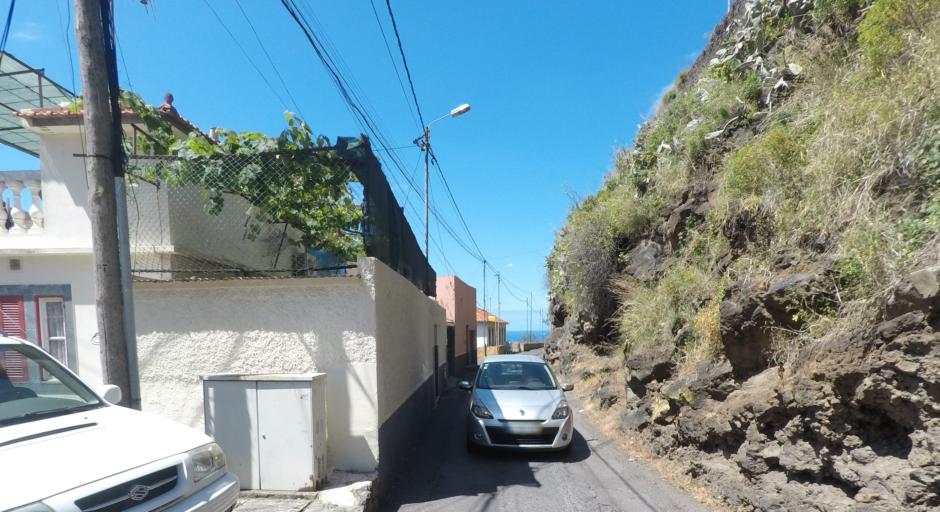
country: PT
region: Madeira
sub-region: Funchal
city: Funchal
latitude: 32.6495
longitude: -16.8865
